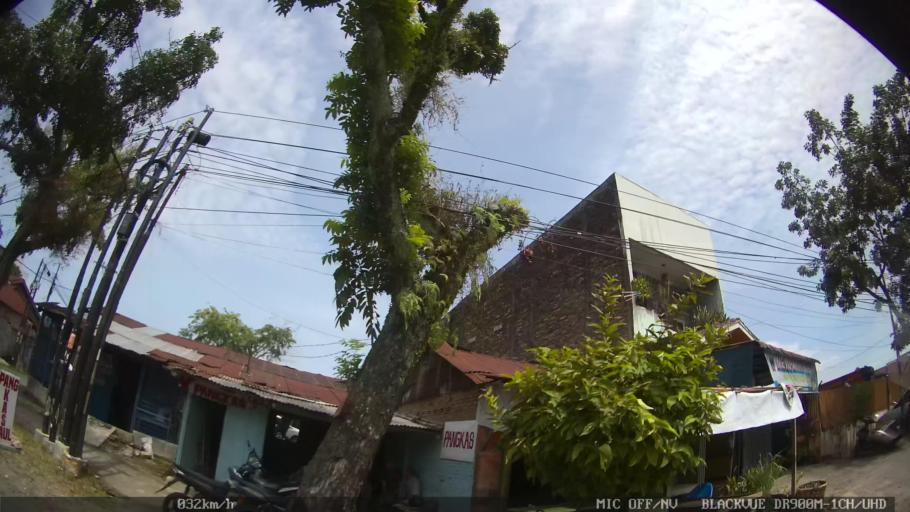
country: ID
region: North Sumatra
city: Sunggal
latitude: 3.5822
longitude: 98.6405
